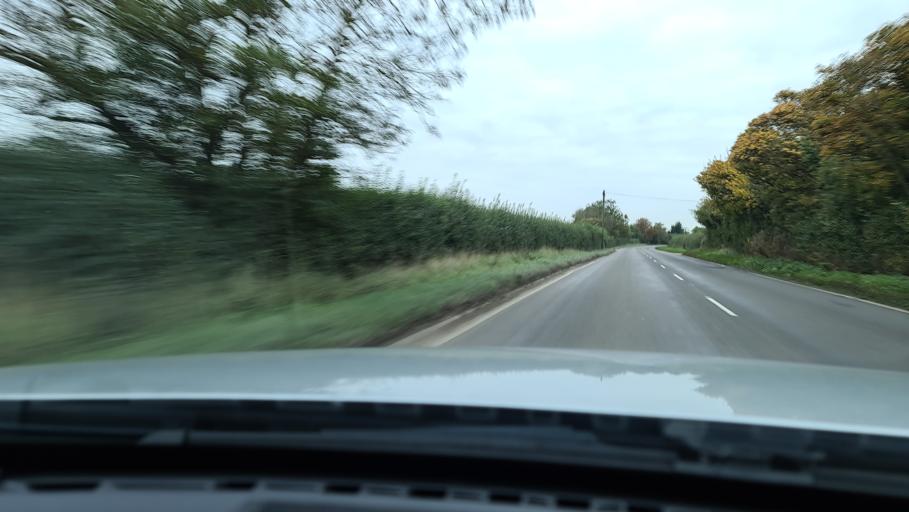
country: GB
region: England
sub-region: Buckinghamshire
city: Waddesdon
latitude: 51.8576
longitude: -0.9810
